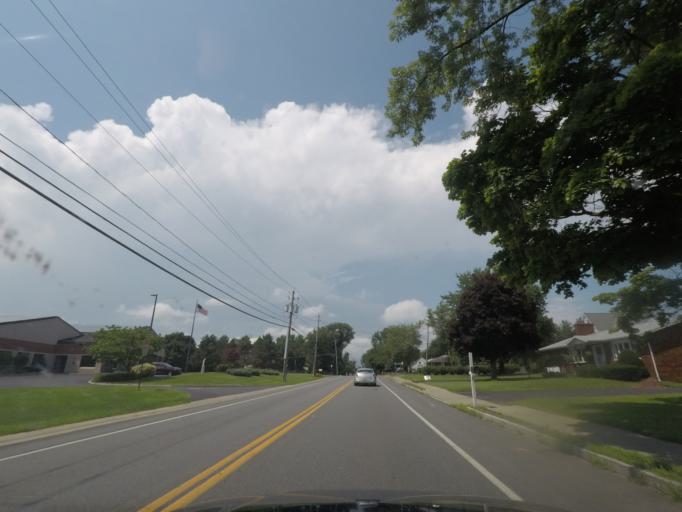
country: US
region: New York
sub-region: Albany County
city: Roessleville
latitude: 42.7149
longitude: -73.7842
